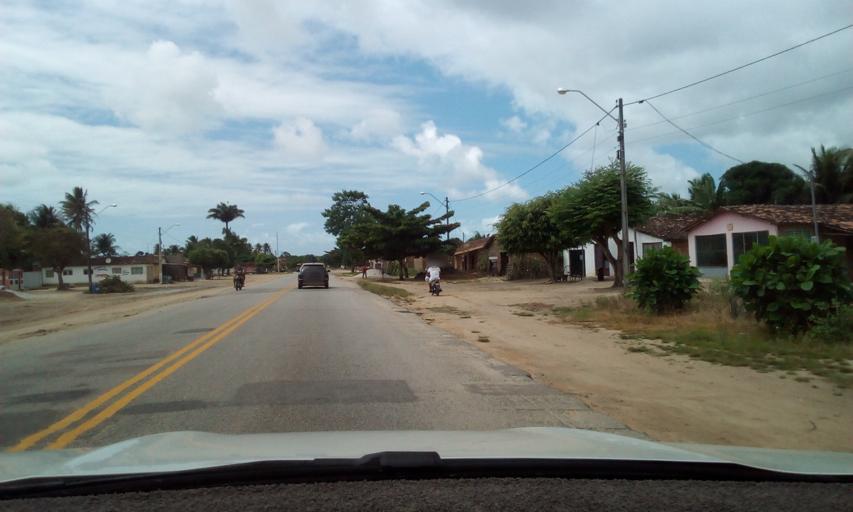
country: BR
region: Paraiba
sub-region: Rio Tinto
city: Rio Tinto
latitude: -6.7703
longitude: -35.0179
